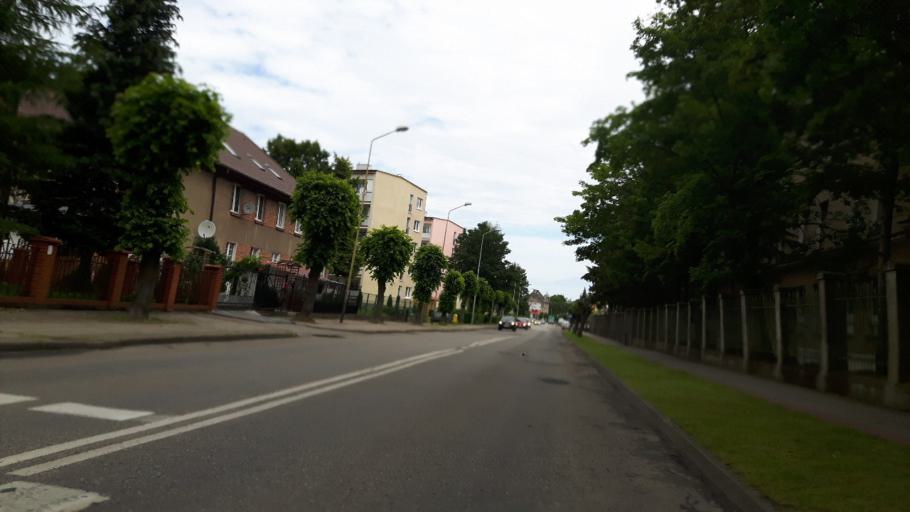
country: PL
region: West Pomeranian Voivodeship
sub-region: Powiat gryficki
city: Trzebiatow
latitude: 54.0539
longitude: 15.2577
